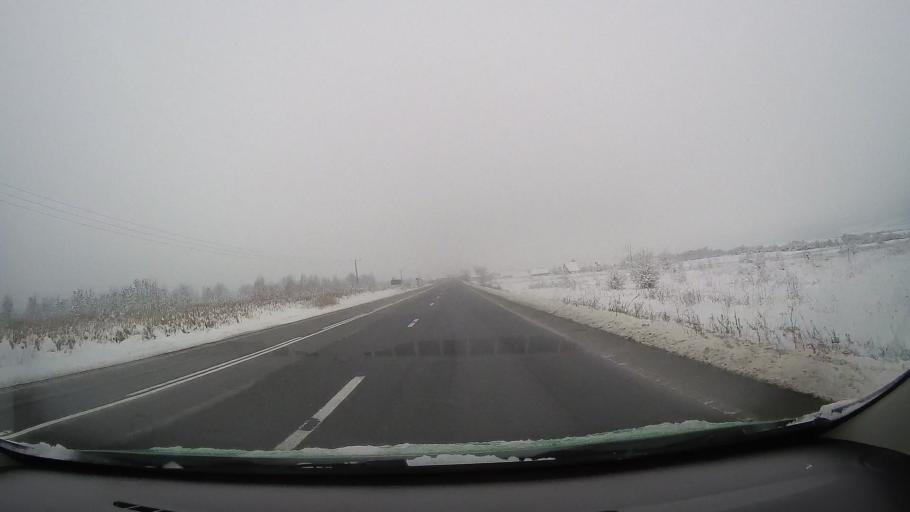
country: RO
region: Sibiu
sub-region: Oras Saliste
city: Saliste
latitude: 45.7882
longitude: 23.9288
